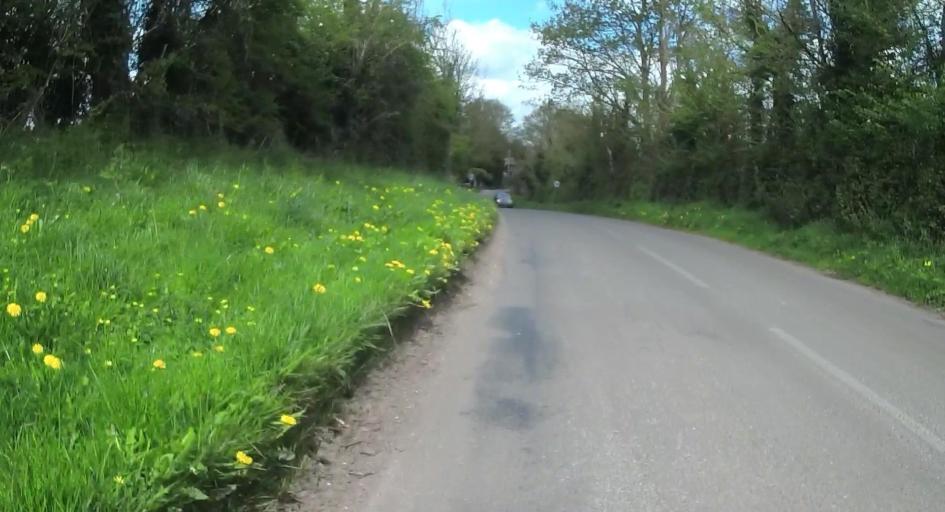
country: GB
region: England
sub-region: Hampshire
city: Abbotts Ann
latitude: 51.1262
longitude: -1.4936
